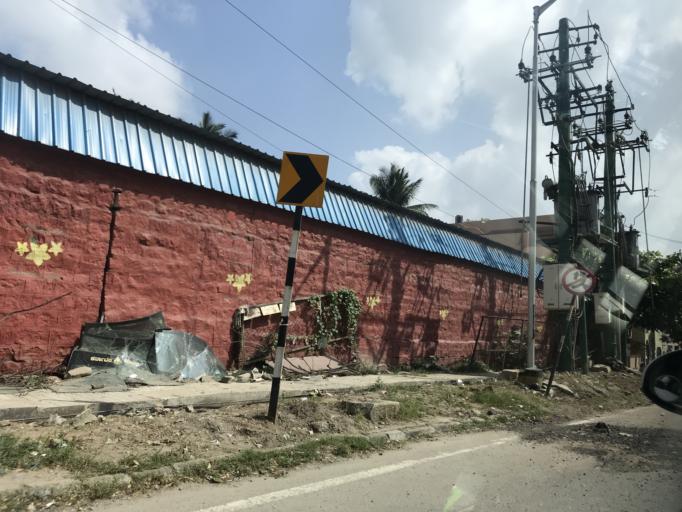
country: IN
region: Karnataka
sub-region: Bangalore Urban
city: Bangalore
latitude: 12.9788
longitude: 77.5646
